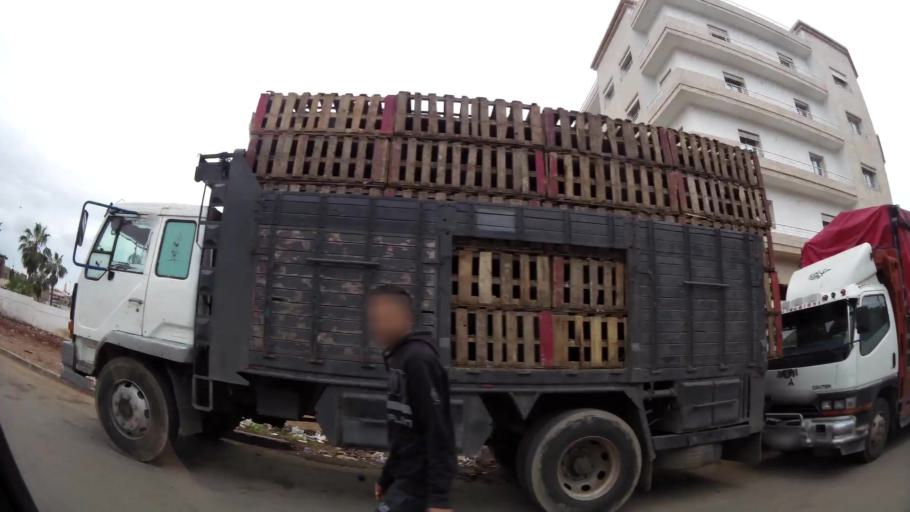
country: MA
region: Grand Casablanca
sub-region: Mediouna
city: Tit Mellil
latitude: 33.5672
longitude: -7.5450
